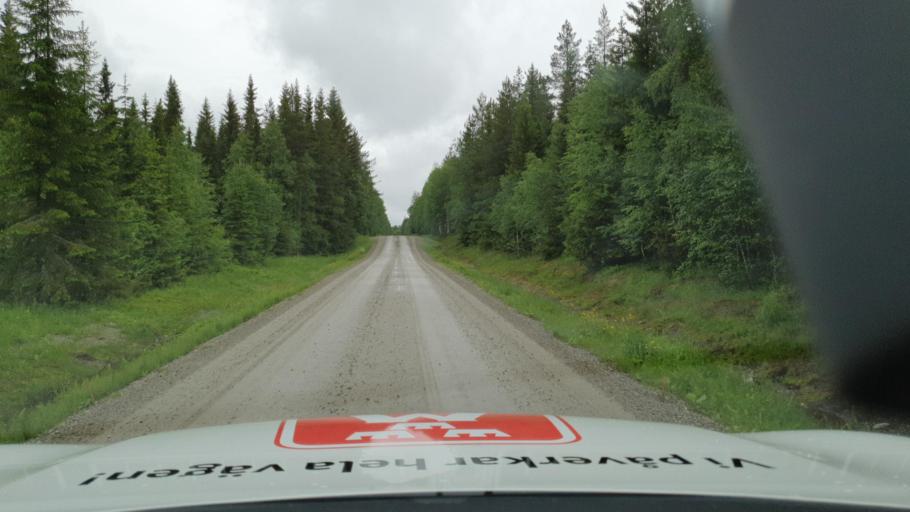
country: SE
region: Vaesterbotten
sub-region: Dorotea Kommun
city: Dorotea
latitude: 63.9924
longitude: 16.8025
